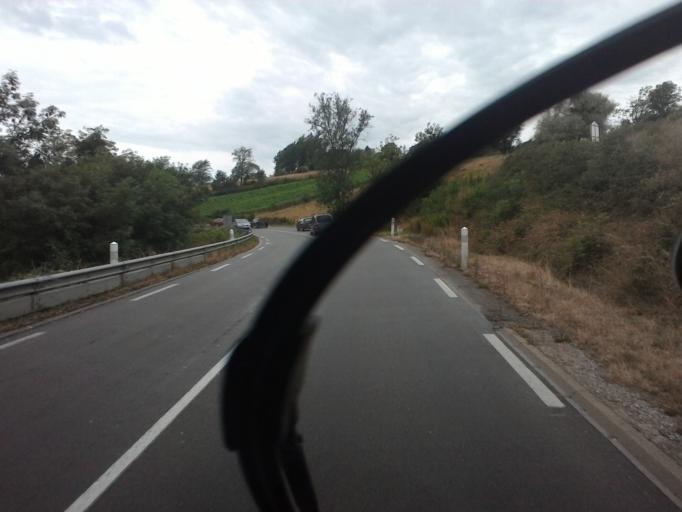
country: FR
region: Franche-Comte
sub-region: Departement du Jura
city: Poligny
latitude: 46.8844
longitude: 5.7260
